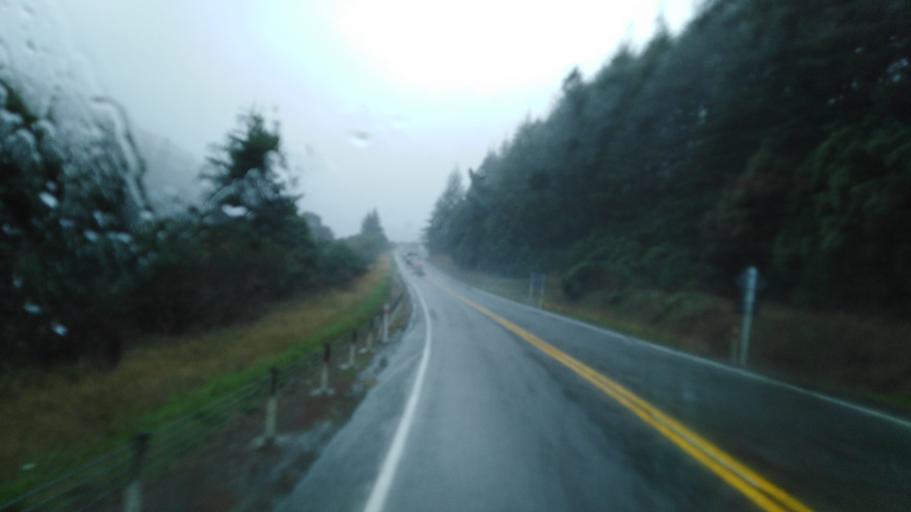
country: NZ
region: Nelson
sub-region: Nelson City
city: Nelson
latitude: -41.2002
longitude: 173.4718
